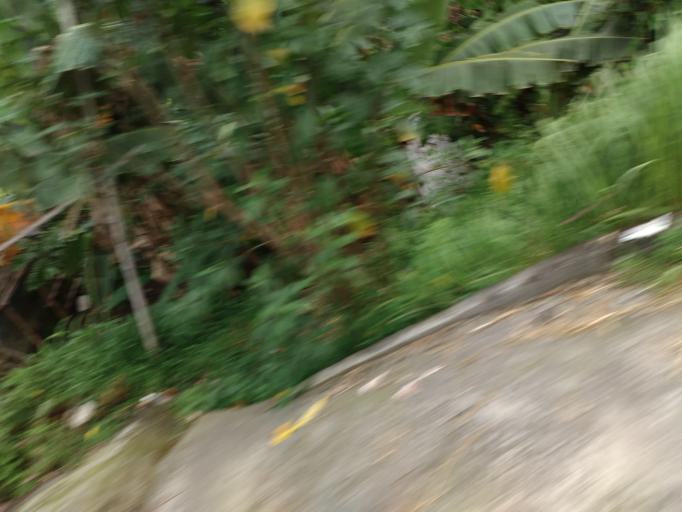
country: ID
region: Central Java
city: Delanggu
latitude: -7.5841
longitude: 110.6483
